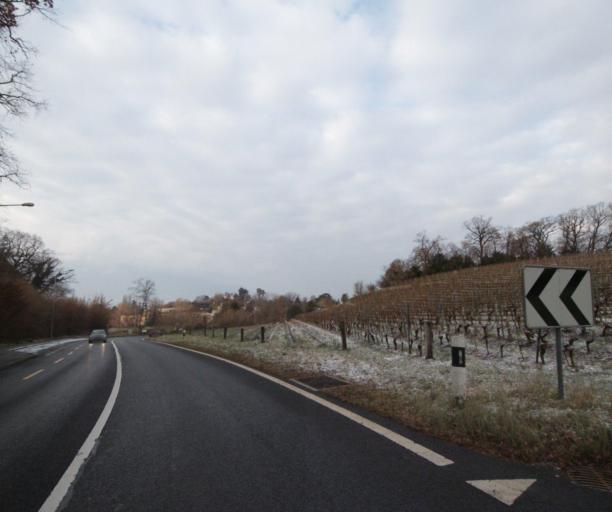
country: CH
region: Vaud
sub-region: Riviera-Pays-d'Enhaut District
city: Le Chatelard
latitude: 46.4517
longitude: 6.8827
